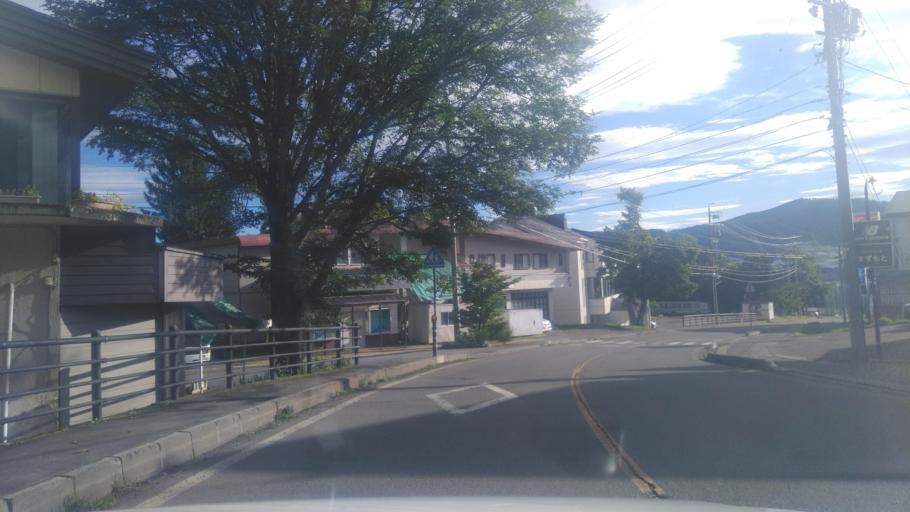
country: JP
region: Nagano
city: Suzaka
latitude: 36.5318
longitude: 138.3436
